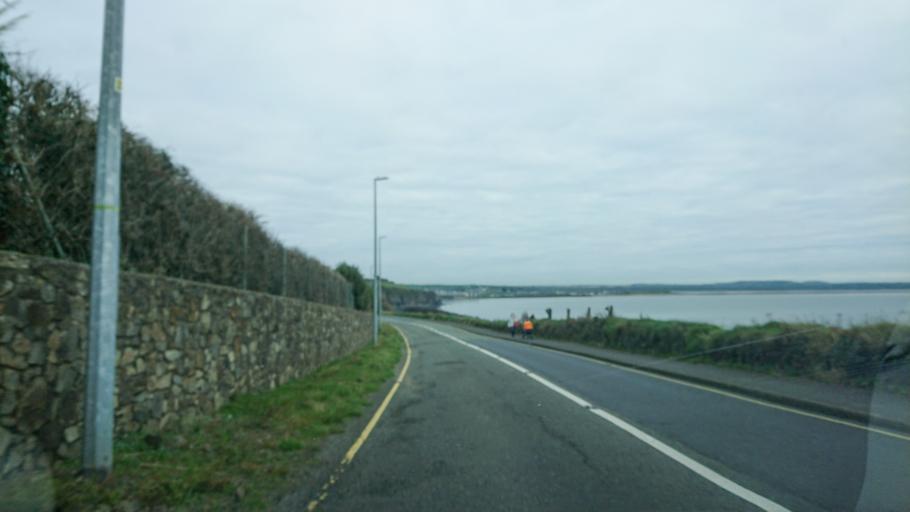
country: IE
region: Munster
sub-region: Waterford
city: Tra Mhor
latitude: 52.1494
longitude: -7.1634
